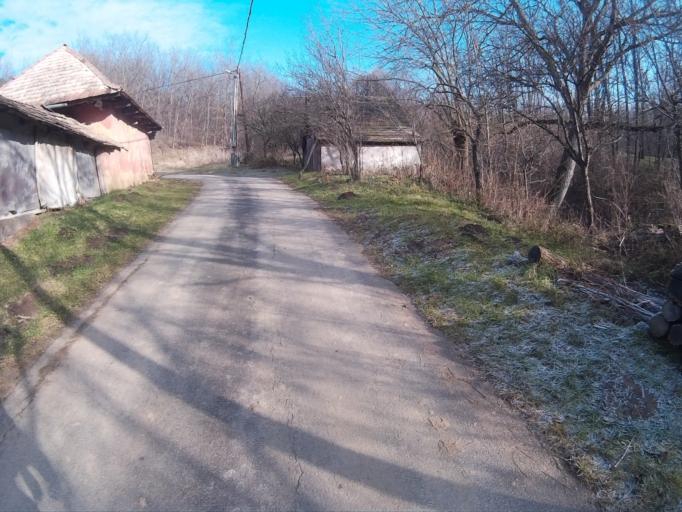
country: HU
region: Nograd
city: Bercel
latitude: 47.9476
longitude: 19.4454
